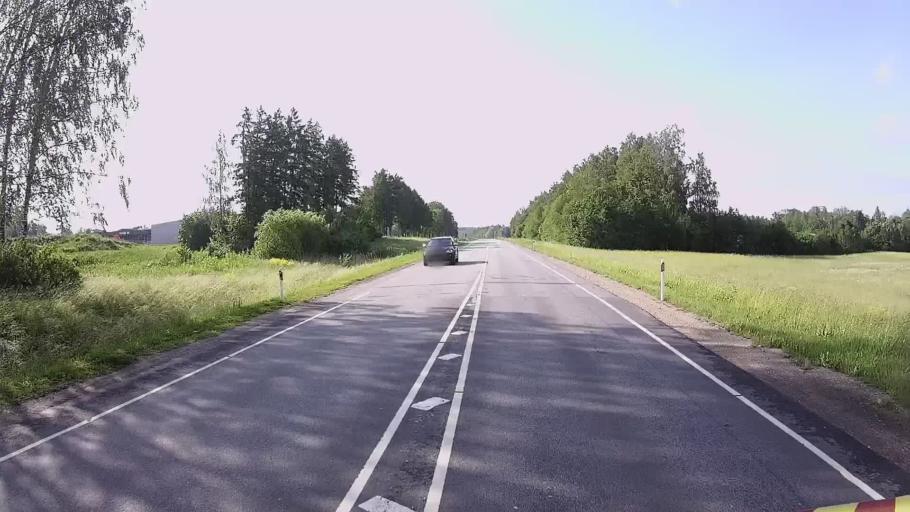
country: EE
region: Viljandimaa
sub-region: Viljandi linn
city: Viljandi
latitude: 58.3441
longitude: 25.5658
